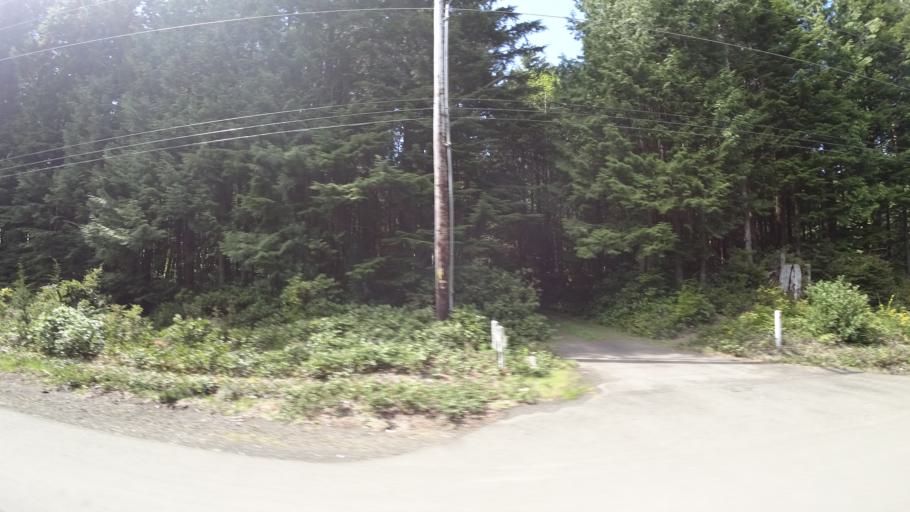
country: US
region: Oregon
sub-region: Lincoln County
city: Lincoln Beach
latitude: 44.8329
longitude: -124.0555
